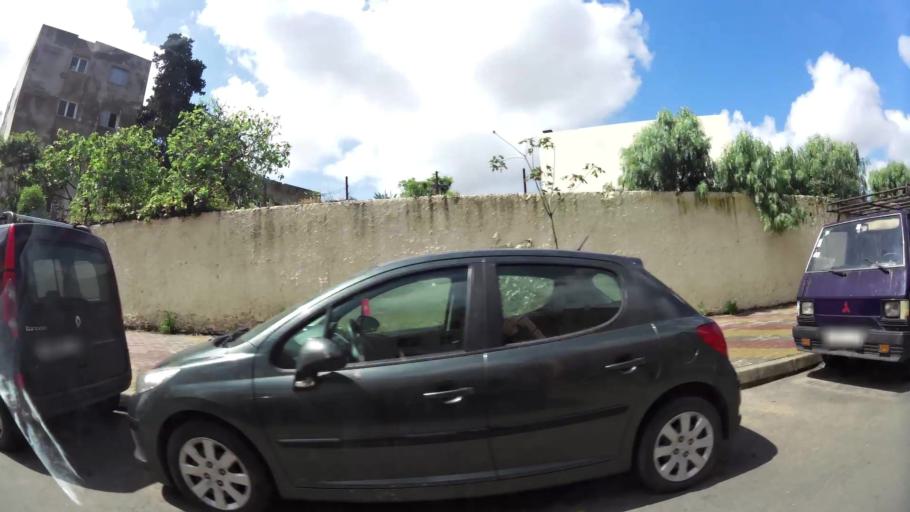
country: MA
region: Grand Casablanca
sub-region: Casablanca
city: Casablanca
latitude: 33.5599
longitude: -7.6040
